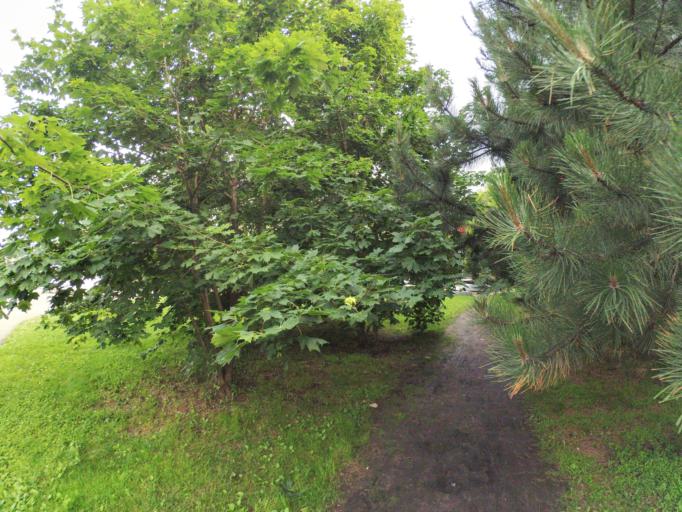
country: RU
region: Moscow
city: Shchukino
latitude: 55.7797
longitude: 37.4438
